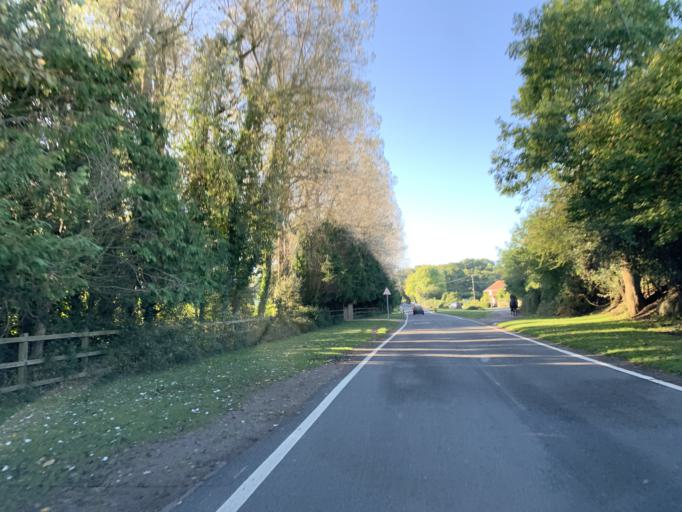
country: GB
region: England
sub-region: Hampshire
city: Cadnam
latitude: 50.9442
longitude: -1.6177
